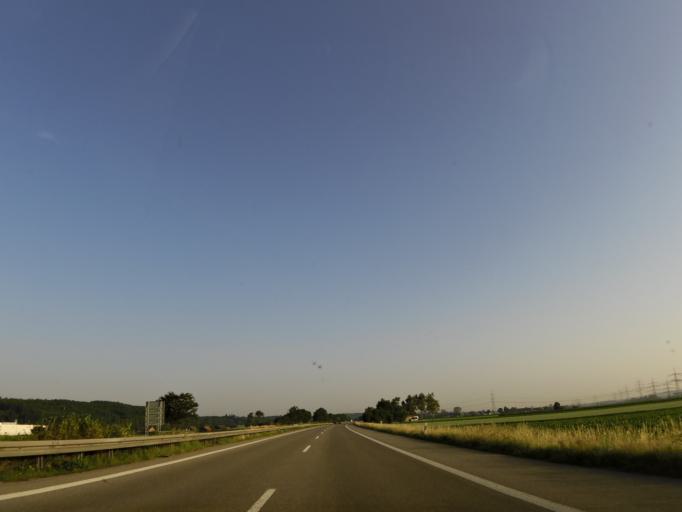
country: DE
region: Bavaria
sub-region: Swabia
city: Woringen
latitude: 47.9273
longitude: 10.2111
